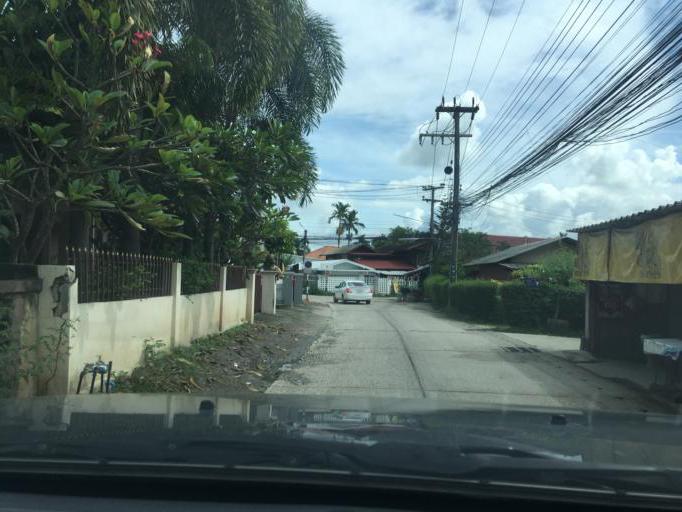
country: TH
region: Chiang Mai
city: San Sai
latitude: 18.8783
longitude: 98.9700
